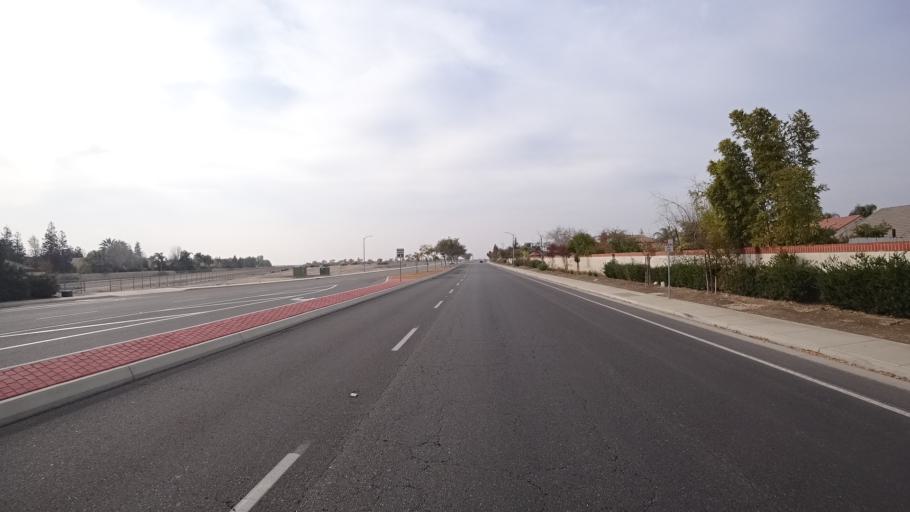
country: US
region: California
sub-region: Kern County
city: Rosedale
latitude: 35.3400
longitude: -119.1405
